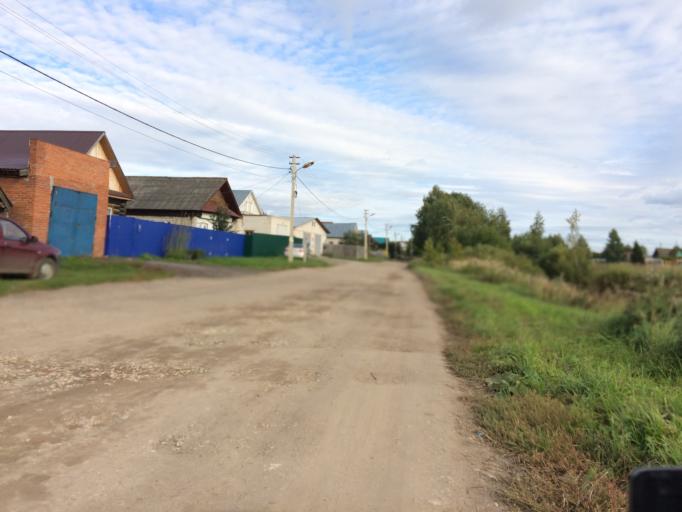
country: RU
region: Mariy-El
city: Yoshkar-Ola
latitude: 56.6551
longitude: 48.0101
